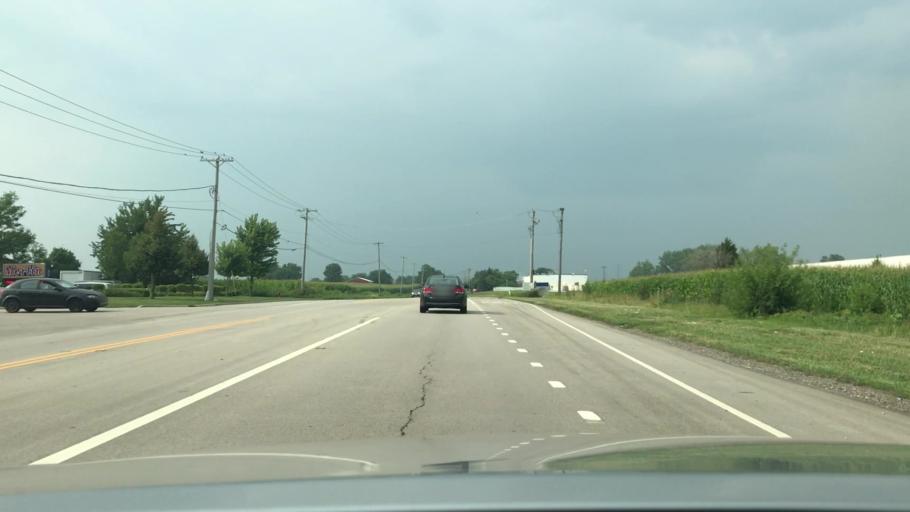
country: US
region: Illinois
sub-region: Will County
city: Plainfield
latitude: 41.6250
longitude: -88.2220
